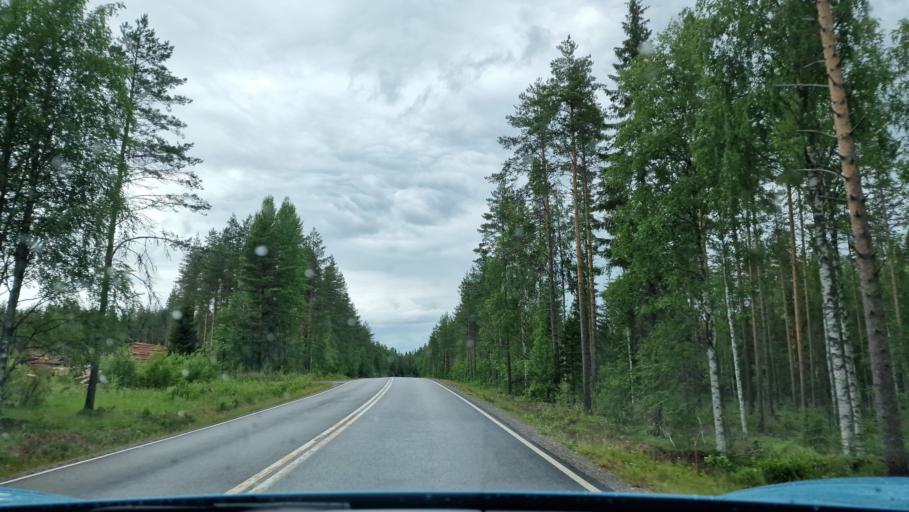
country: FI
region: Central Finland
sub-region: Saarijaervi-Viitasaari
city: Pylkoenmaeki
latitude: 62.6151
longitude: 24.5825
